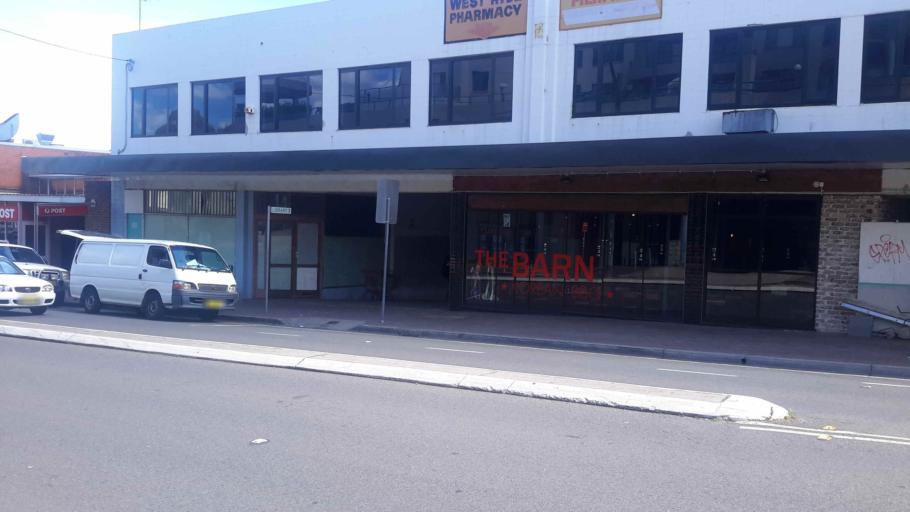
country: AU
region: New South Wales
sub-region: Ryde
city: Denistone
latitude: -33.8071
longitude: 151.0893
